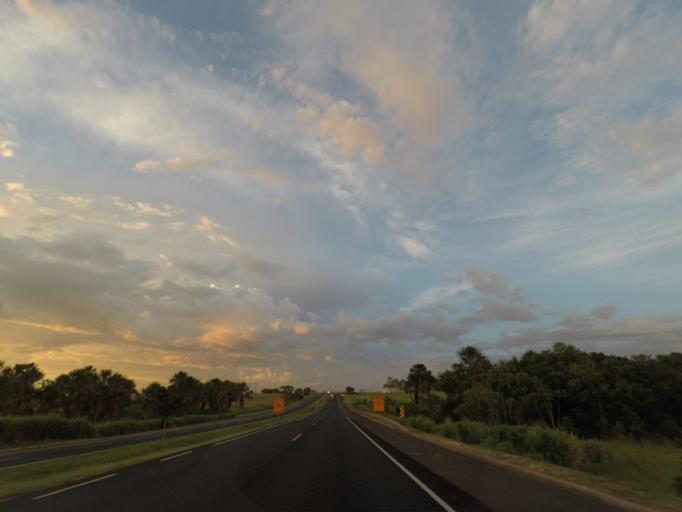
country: BR
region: Minas Gerais
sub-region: Uberaba
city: Uberaba
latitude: -19.6349
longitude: -48.0119
